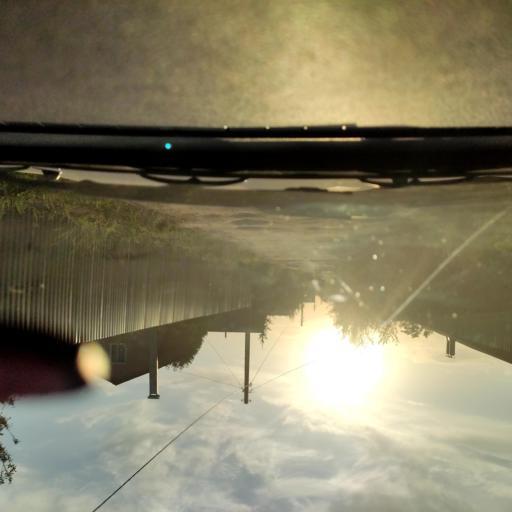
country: RU
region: Voronezj
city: Podgornoye
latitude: 51.8335
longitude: 39.1952
